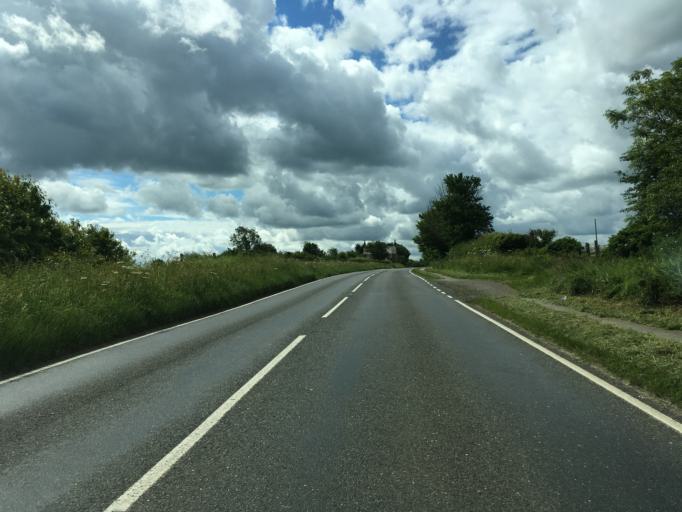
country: GB
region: England
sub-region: Oxfordshire
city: Chipping Norton
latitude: 51.9286
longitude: -1.5414
